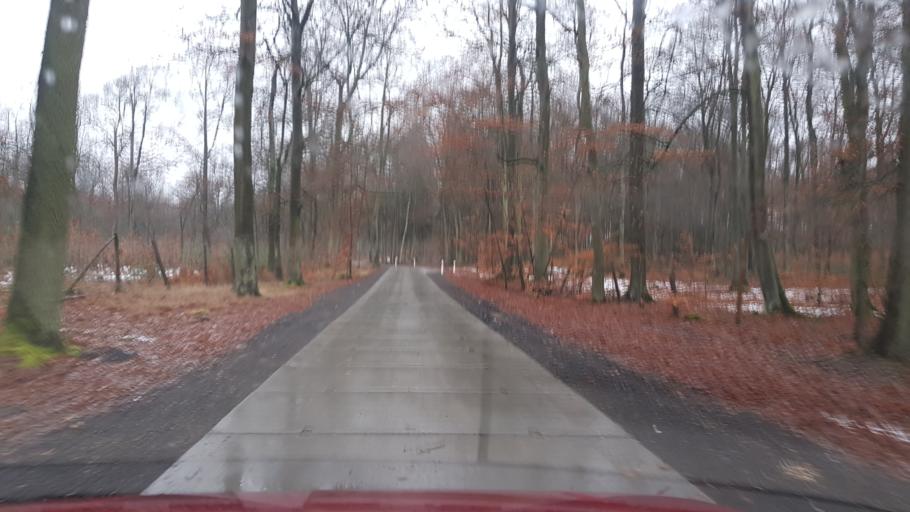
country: PL
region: West Pomeranian Voivodeship
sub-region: Powiat policki
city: Dobra
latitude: 53.5500
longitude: 14.4147
